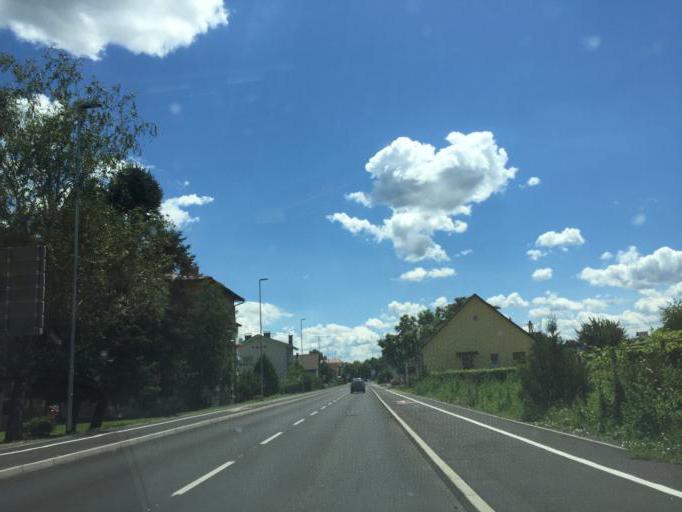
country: AT
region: Styria
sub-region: Politischer Bezirk Suedoststeiermark
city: Bad Radkersburg
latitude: 46.6811
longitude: 15.9897
